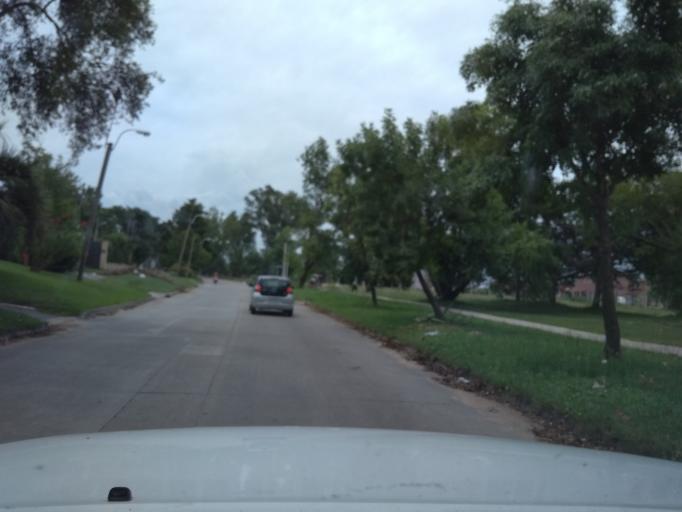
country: UY
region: Canelones
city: Paso de Carrasco
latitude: -34.8723
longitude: -56.0585
